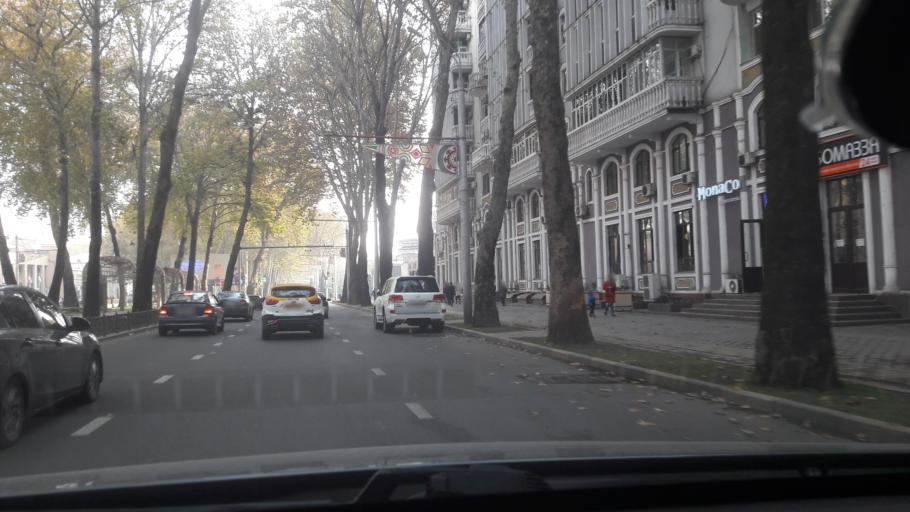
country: TJ
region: Dushanbe
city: Dushanbe
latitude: 38.5723
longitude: 68.7881
